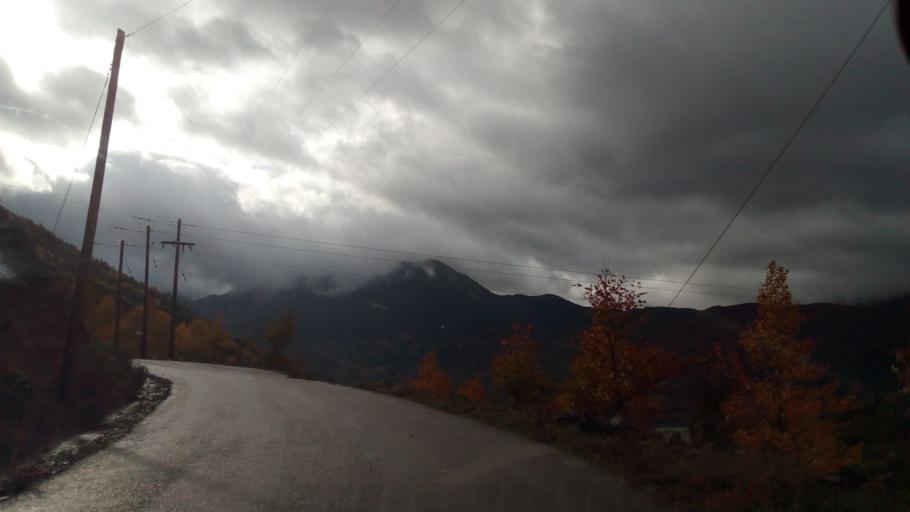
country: GR
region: West Greece
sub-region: Nomos Aitolias kai Akarnanias
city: Thermo
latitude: 38.6807
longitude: 21.8490
